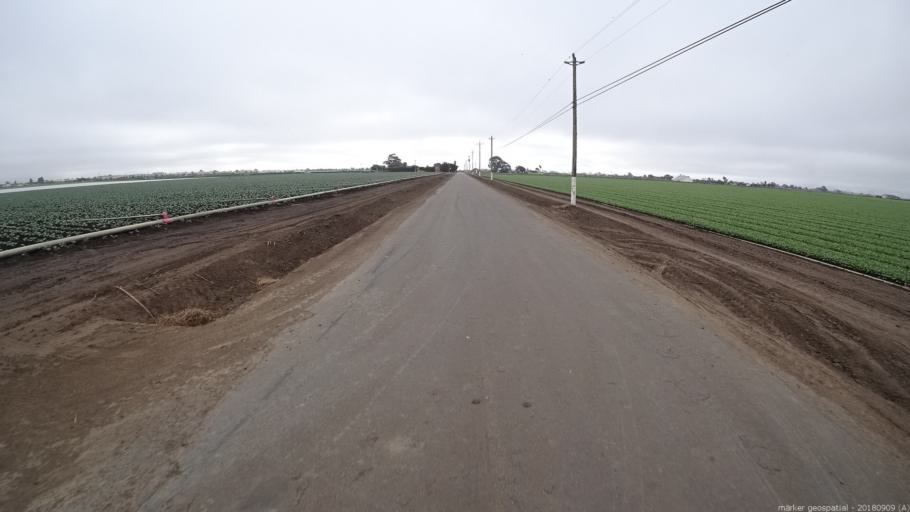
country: US
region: California
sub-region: Monterey County
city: Boronda
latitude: 36.7164
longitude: -121.6801
